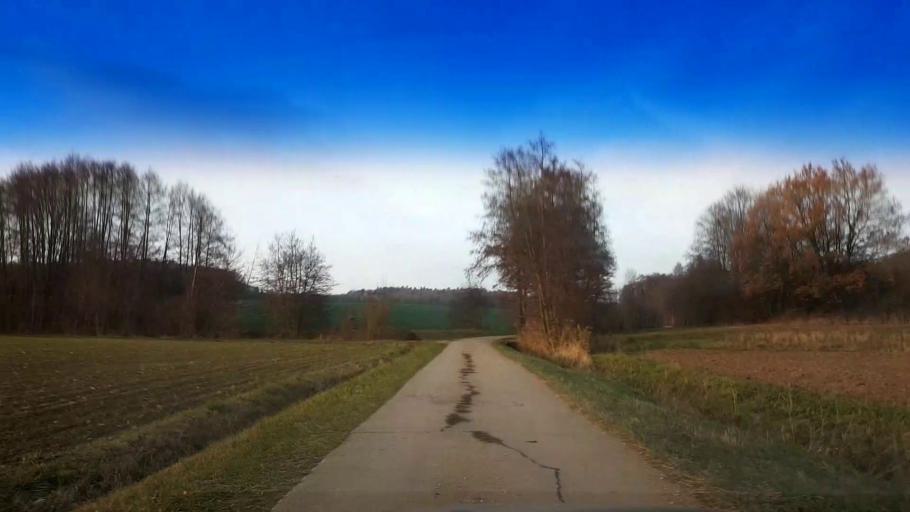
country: DE
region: Bavaria
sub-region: Upper Franconia
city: Schesslitz
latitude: 49.9772
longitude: 10.9856
